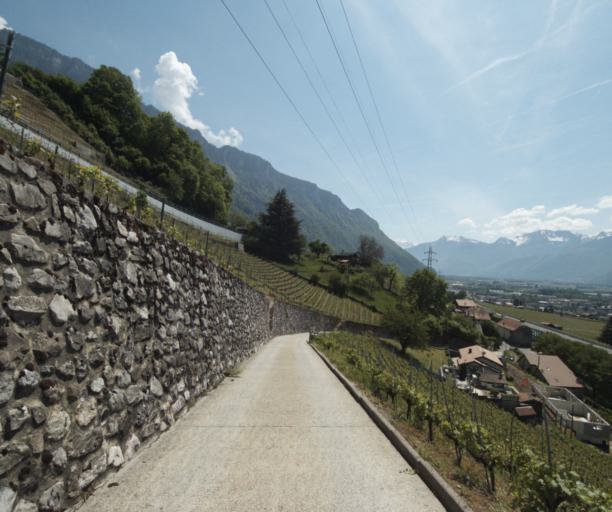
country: CH
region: Vaud
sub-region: Aigle District
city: Villeneuve
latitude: 46.4052
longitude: 6.9352
